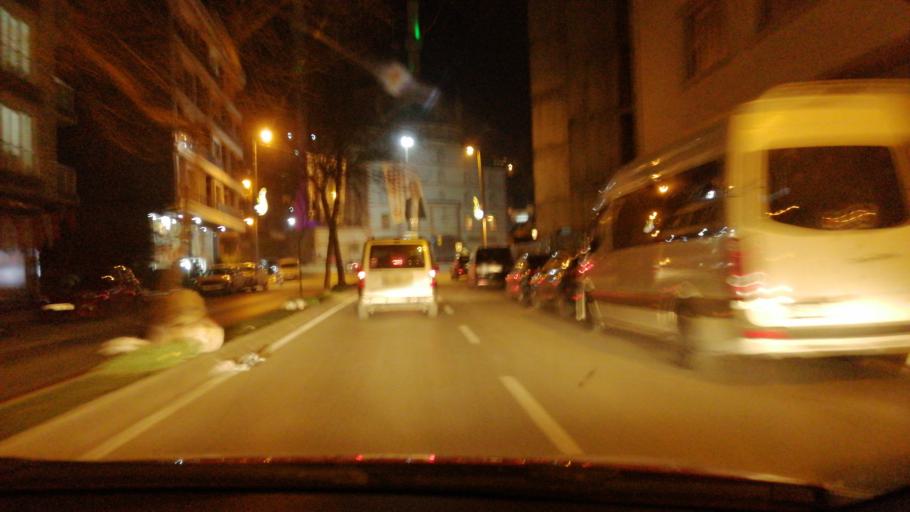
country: TR
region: Istanbul
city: Sisli
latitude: 41.0860
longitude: 28.9735
